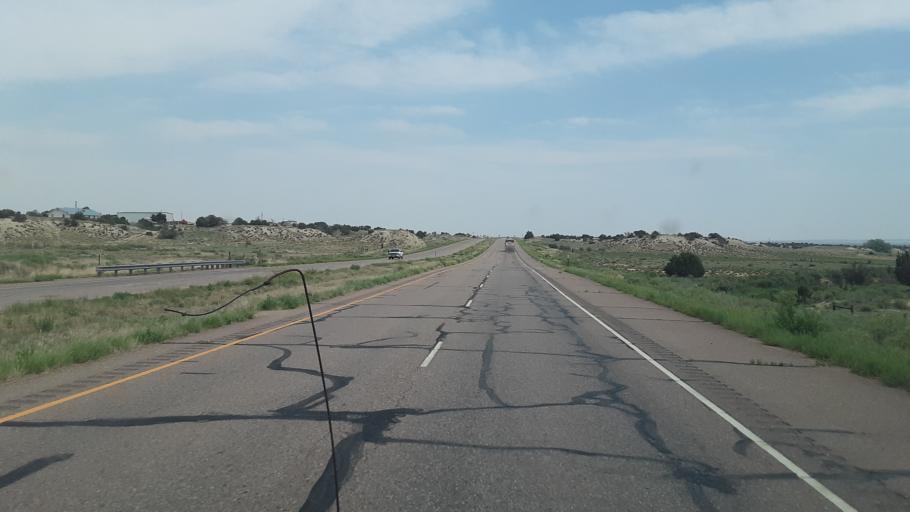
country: US
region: Colorado
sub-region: Fremont County
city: Penrose
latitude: 38.3980
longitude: -104.9773
